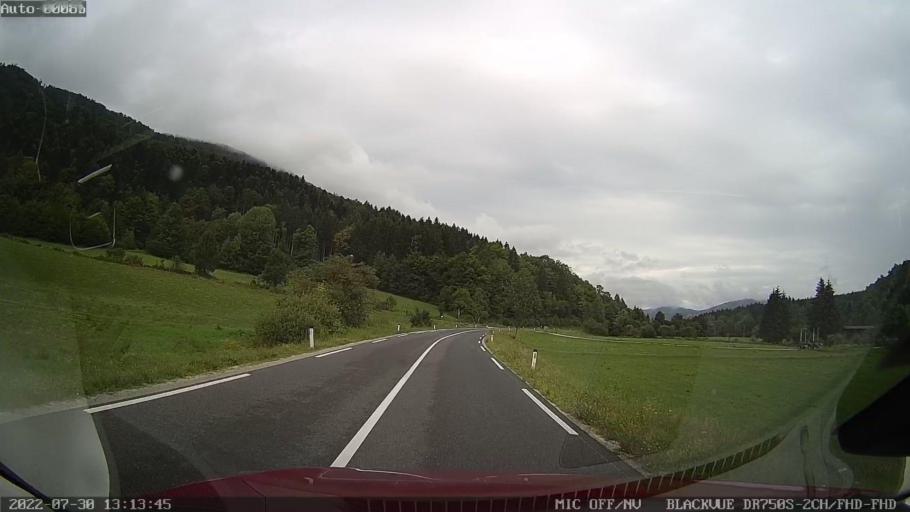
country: SI
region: Dolenjske Toplice
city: Dolenjske Toplice
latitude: 45.7236
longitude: 15.0539
